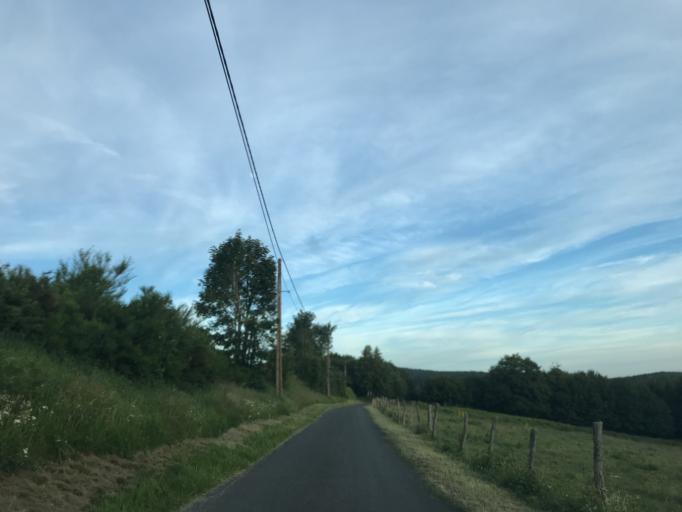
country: FR
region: Rhone-Alpes
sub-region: Departement de la Loire
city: Noiretable
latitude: 45.7721
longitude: 3.7065
